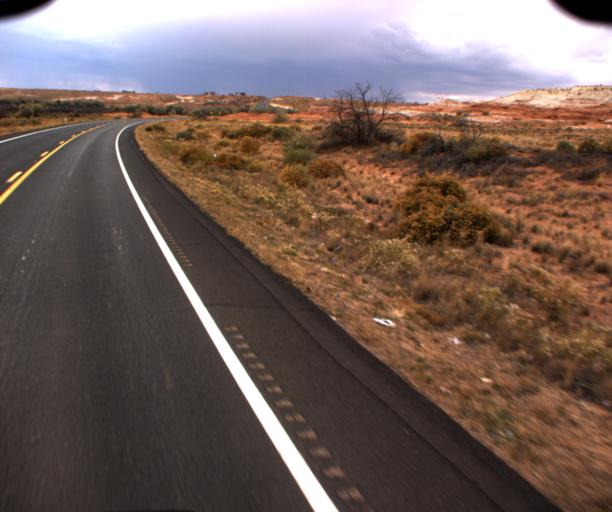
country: US
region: Arizona
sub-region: Coconino County
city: Kaibito
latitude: 36.3269
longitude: -110.9280
